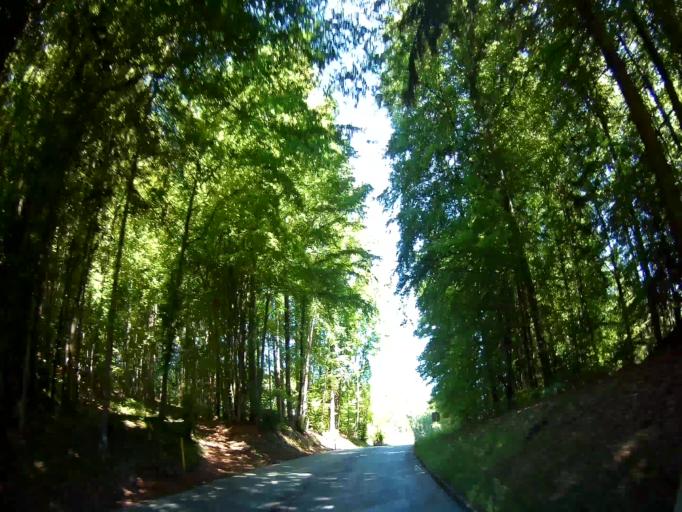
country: AT
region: Carinthia
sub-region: Politischer Bezirk Klagenfurt Land
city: Maria Worth
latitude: 46.5958
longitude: 14.1580
